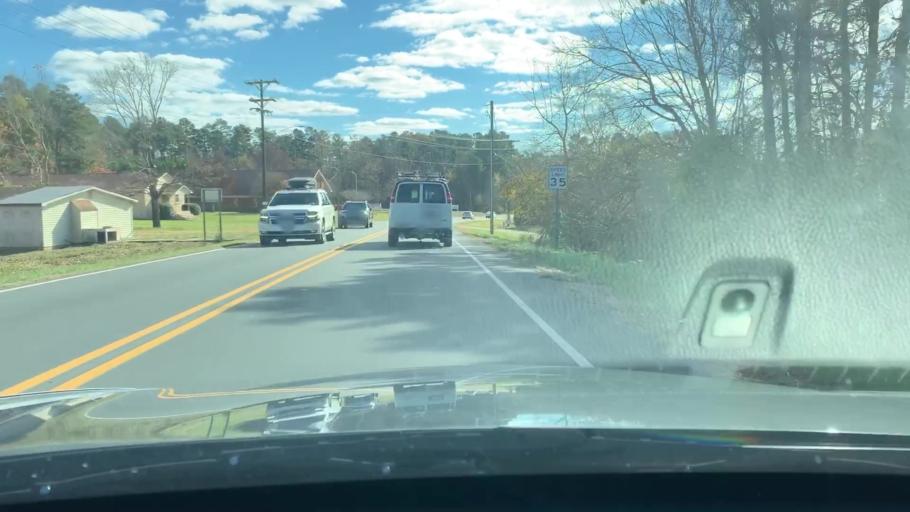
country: US
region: North Carolina
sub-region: Alamance County
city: Haw River
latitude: 36.0976
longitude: -79.3500
